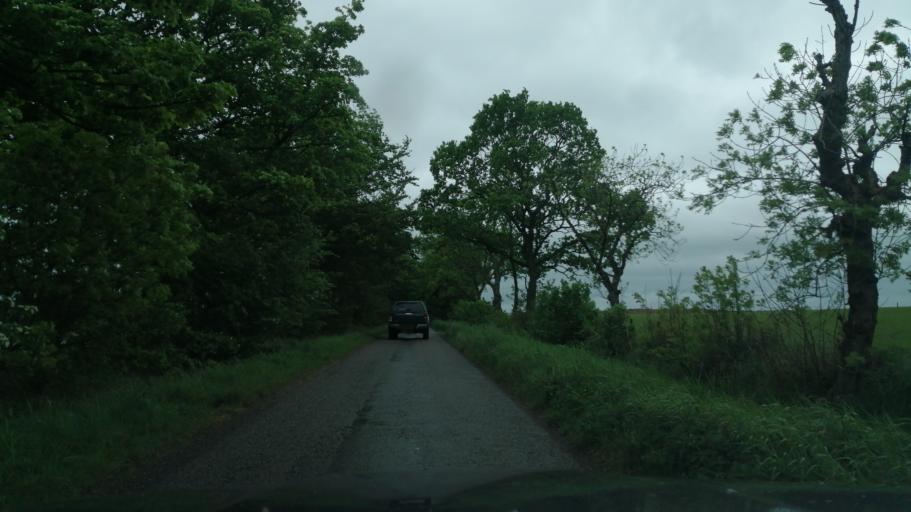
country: GB
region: Scotland
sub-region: Moray
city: Keith
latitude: 57.5701
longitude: -2.8338
